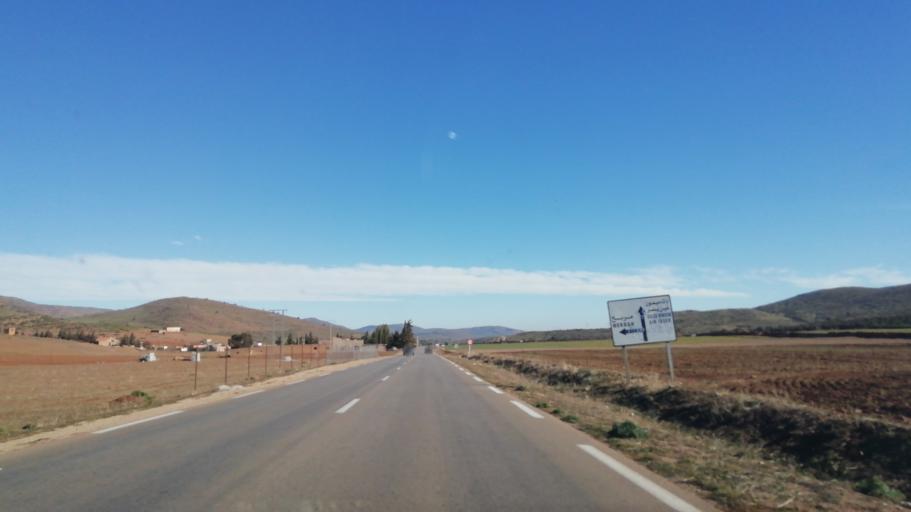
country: DZ
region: Tlemcen
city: Sebdou
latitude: 34.7396
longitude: -1.1703
